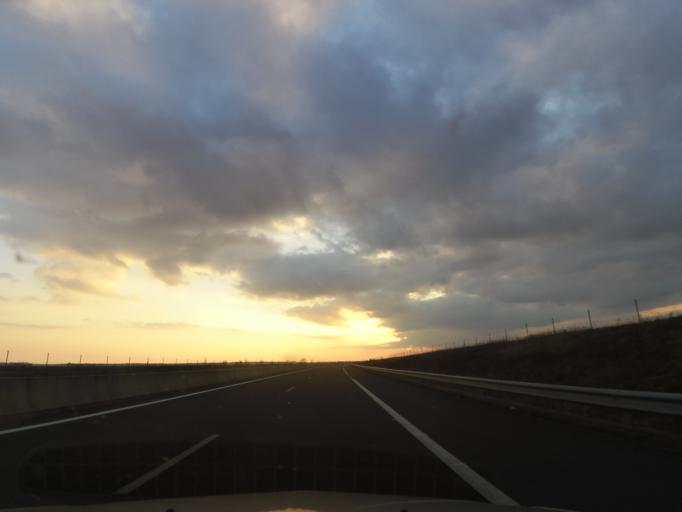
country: FR
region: Centre
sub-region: Departement du Loiret
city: Artenay
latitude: 48.0533
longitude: 1.9352
